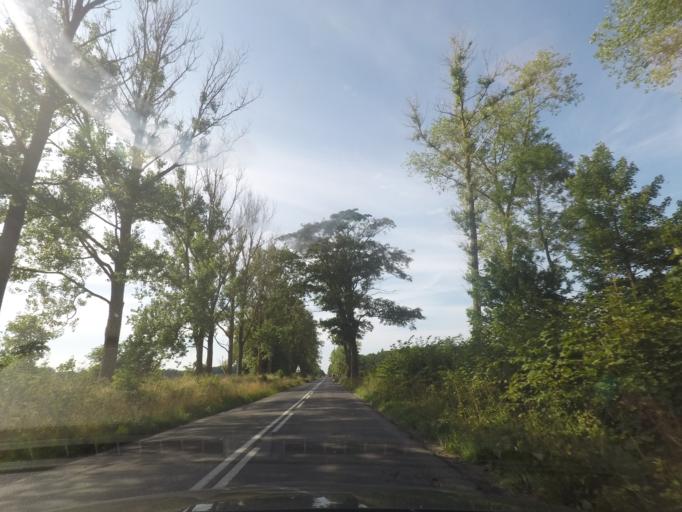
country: PL
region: Pomeranian Voivodeship
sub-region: Powiat leborski
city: Leba
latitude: 54.6893
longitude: 17.5955
